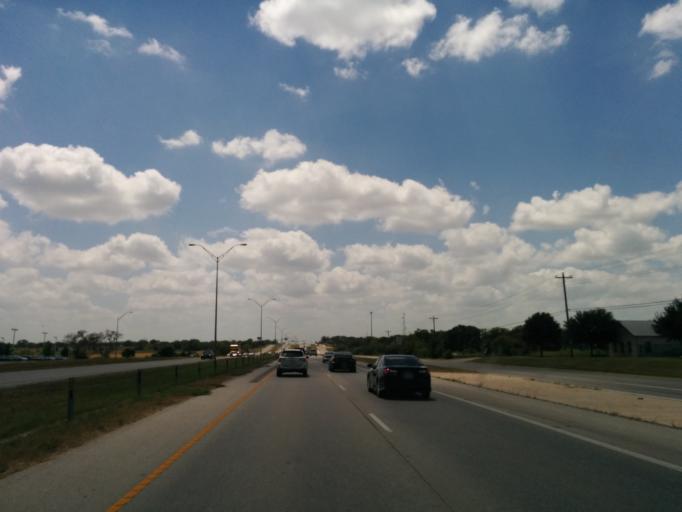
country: US
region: Texas
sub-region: Bastrop County
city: Bastrop
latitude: 30.1112
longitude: -97.3565
